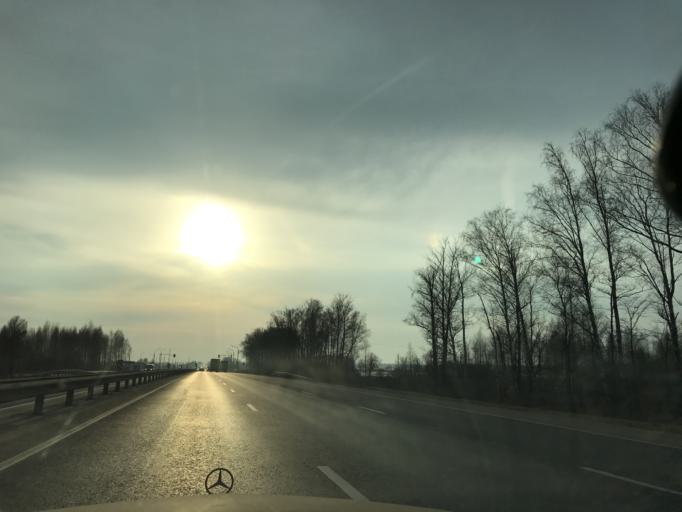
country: RU
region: Vladimir
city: Vorsha
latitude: 56.0708
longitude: 40.1610
